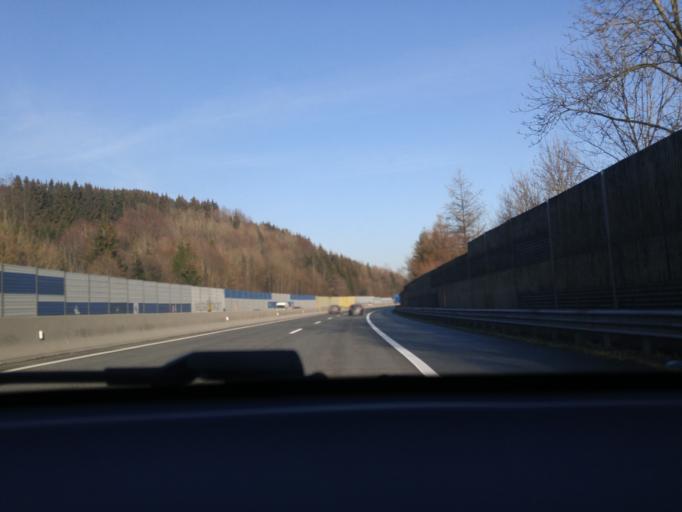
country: AT
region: Upper Austria
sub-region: Politischer Bezirk Vocklabruck
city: Sankt Georgen im Attergau
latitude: 47.9094
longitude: 13.4511
